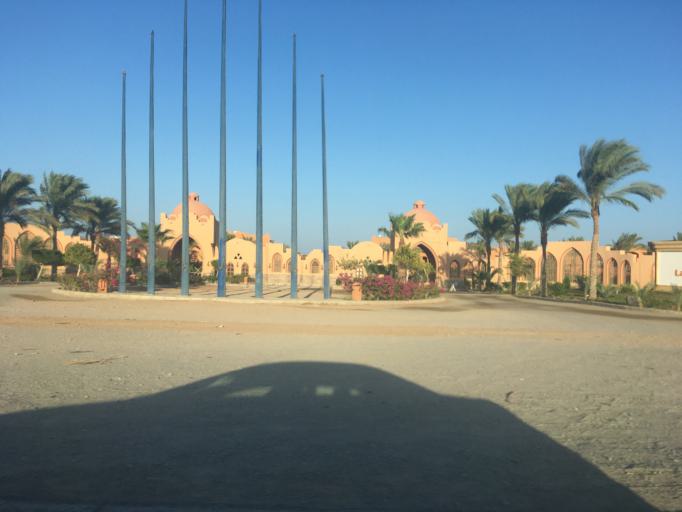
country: EG
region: Red Sea
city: Marsa Alam
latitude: 24.9125
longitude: 34.9646
